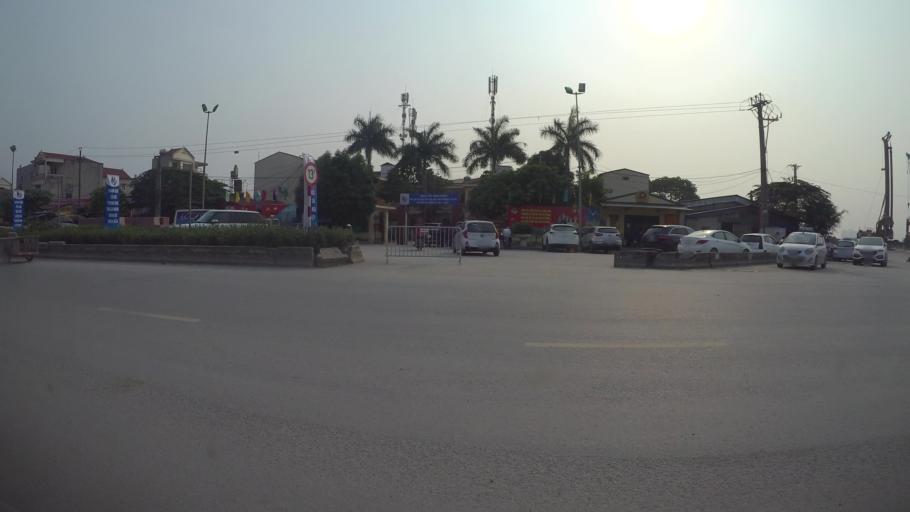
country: VN
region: Ha Noi
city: Cau Dien
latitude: 21.0061
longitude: 105.7490
